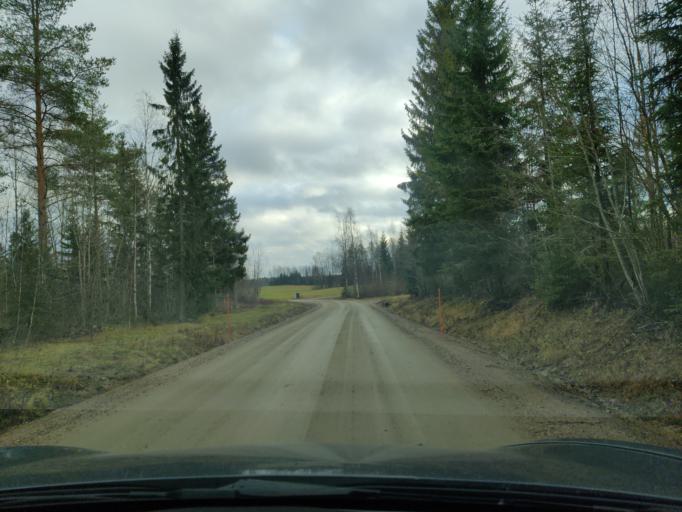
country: FI
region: Northern Savo
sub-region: Ylae-Savo
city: Kiuruvesi
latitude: 63.6380
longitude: 26.6468
